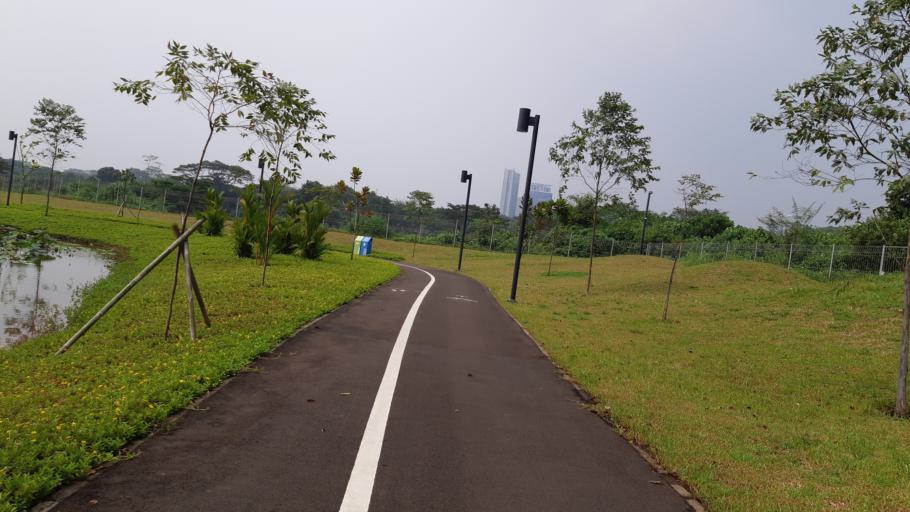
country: ID
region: West Java
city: Serpong
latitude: -6.2935
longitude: 106.6534
